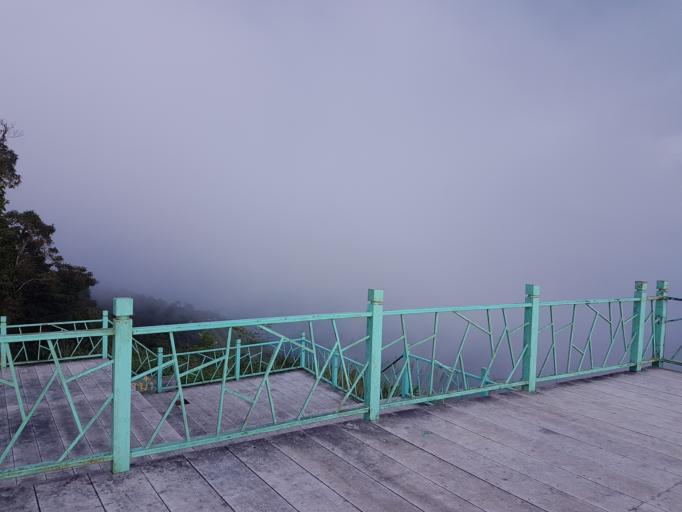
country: TH
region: Phetchabun
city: Lom Kao
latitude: 16.8914
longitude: 101.0940
